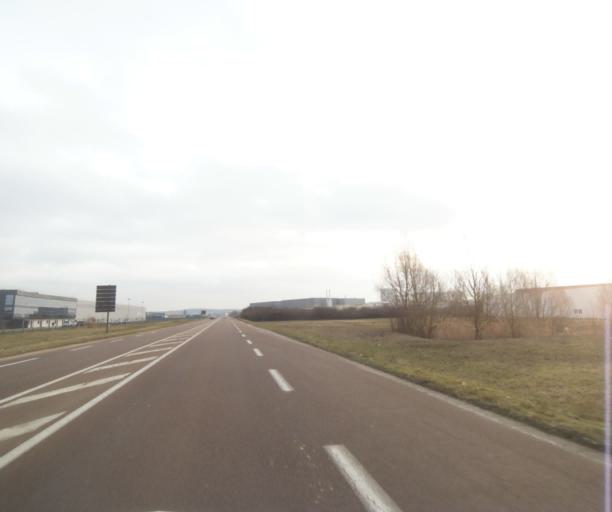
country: FR
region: Champagne-Ardenne
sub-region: Departement de la Haute-Marne
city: Saint-Dizier
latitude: 48.6485
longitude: 4.9381
